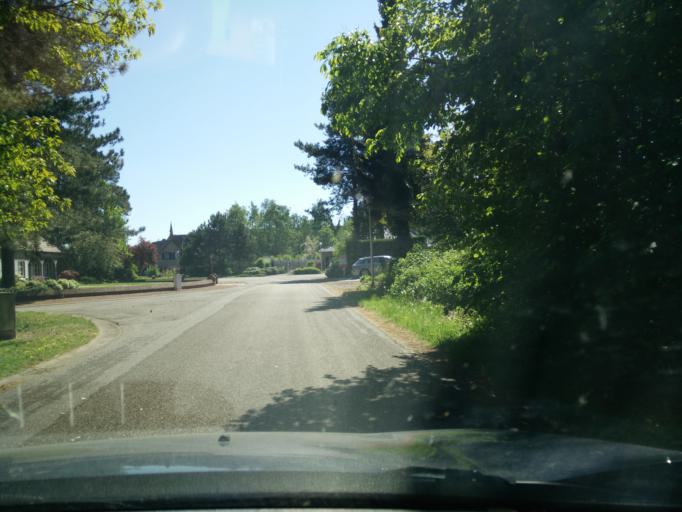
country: BE
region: Flanders
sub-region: Provincie Limburg
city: Maasmechelen
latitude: 50.9942
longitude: 5.6821
